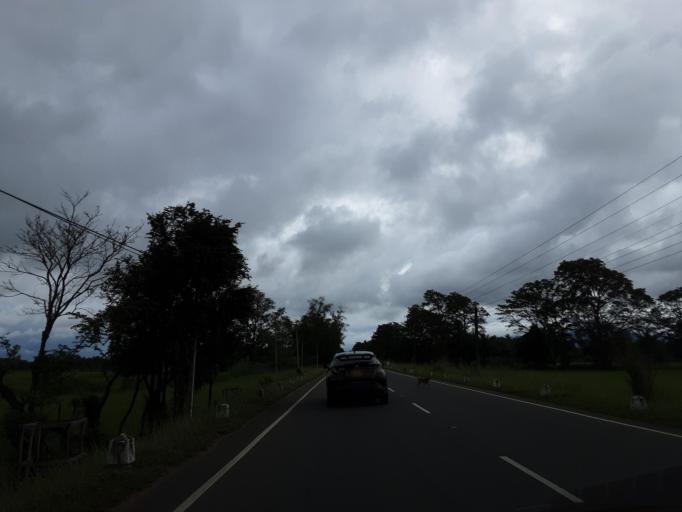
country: LK
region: Uva
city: Badulla
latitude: 7.3720
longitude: 81.0656
